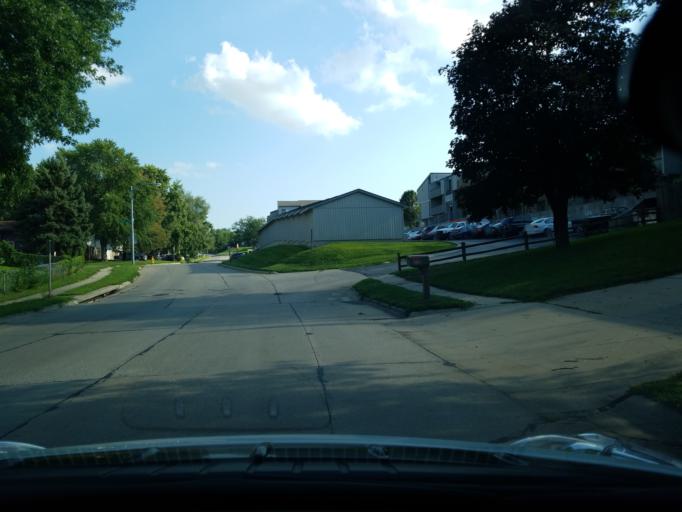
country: US
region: Nebraska
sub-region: Sarpy County
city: Offutt Air Force Base
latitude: 41.1330
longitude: -95.9639
